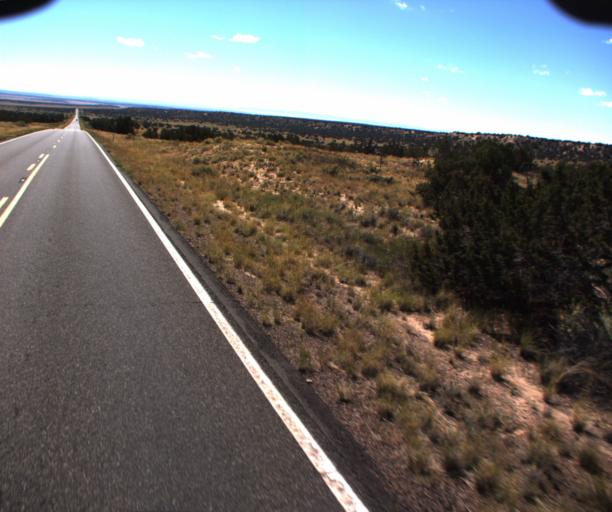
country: US
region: Arizona
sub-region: Apache County
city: Saint Johns
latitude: 34.8175
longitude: -109.2376
